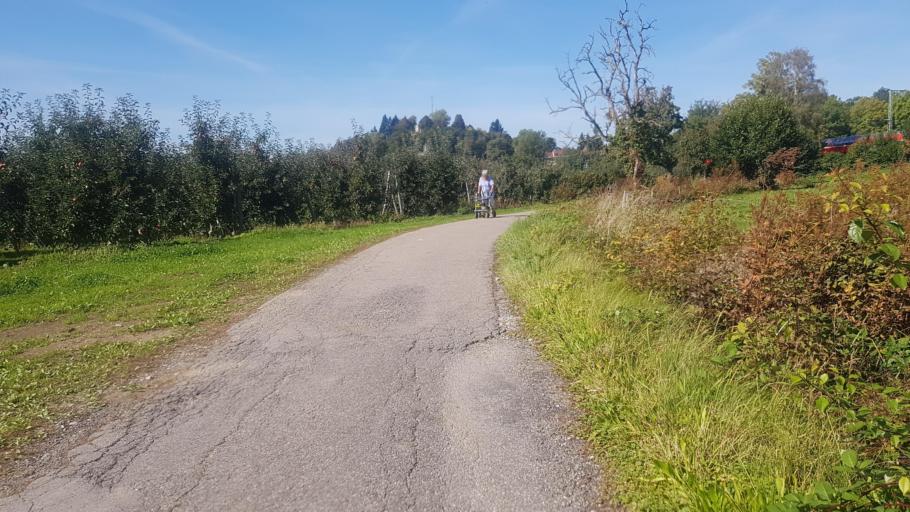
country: DE
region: Bavaria
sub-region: Swabia
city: Lindau
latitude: 47.5609
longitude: 9.6823
